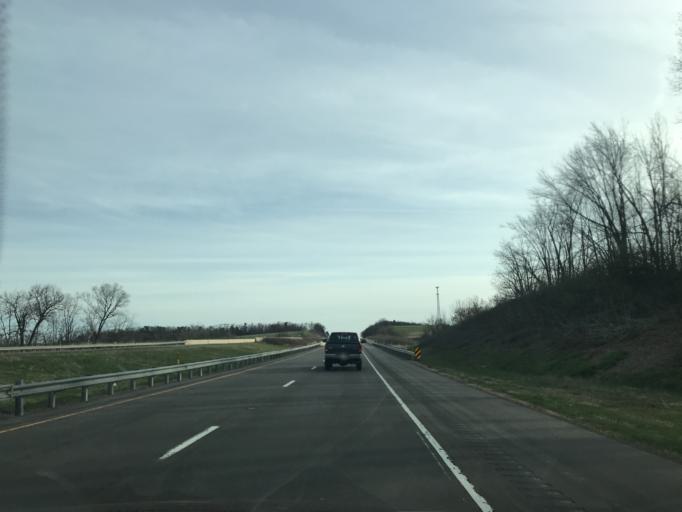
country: US
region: Pennsylvania
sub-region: Northumberland County
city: Watsontown
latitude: 41.0766
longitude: -76.8255
